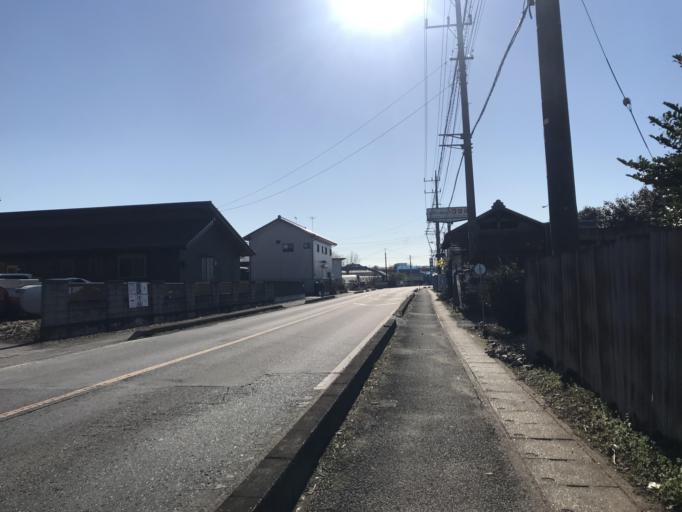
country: JP
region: Ibaraki
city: Sakai
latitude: 36.1295
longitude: 139.8014
